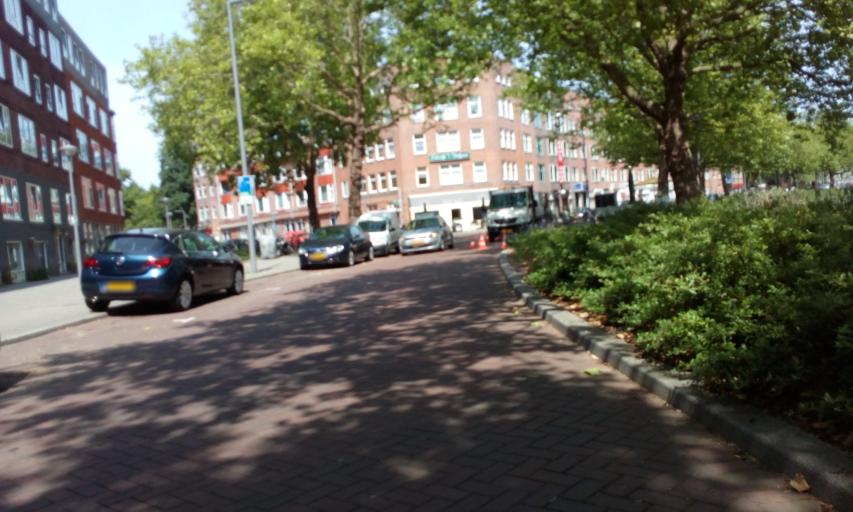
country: NL
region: South Holland
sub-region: Gemeente Rotterdam
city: Rotterdam
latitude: 51.9380
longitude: 4.4859
